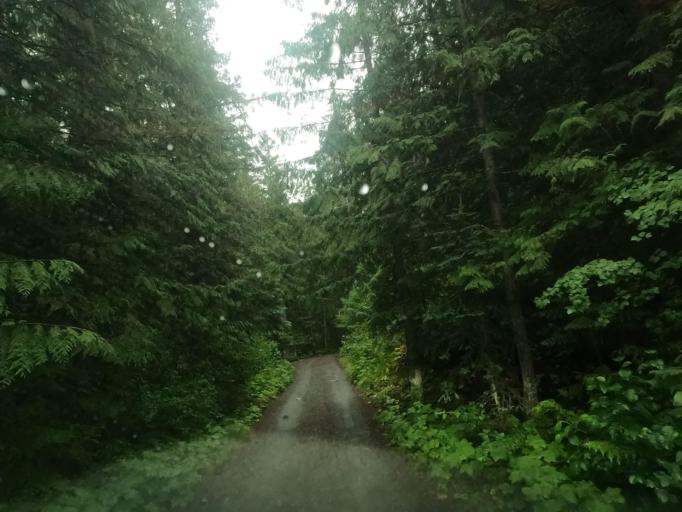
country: CA
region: British Columbia
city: Lillooet
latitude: 50.5296
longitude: -122.1562
